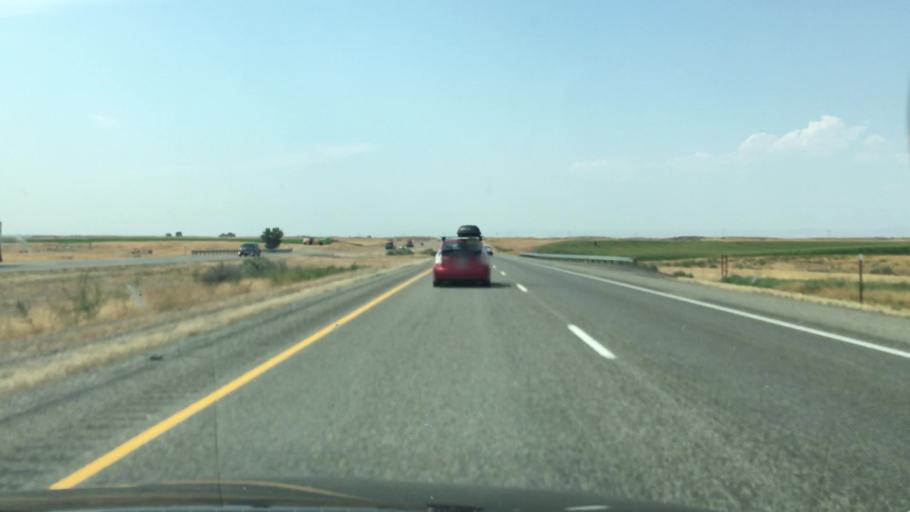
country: US
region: Idaho
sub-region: Gooding County
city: Wendell
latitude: 42.8120
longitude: -114.7762
